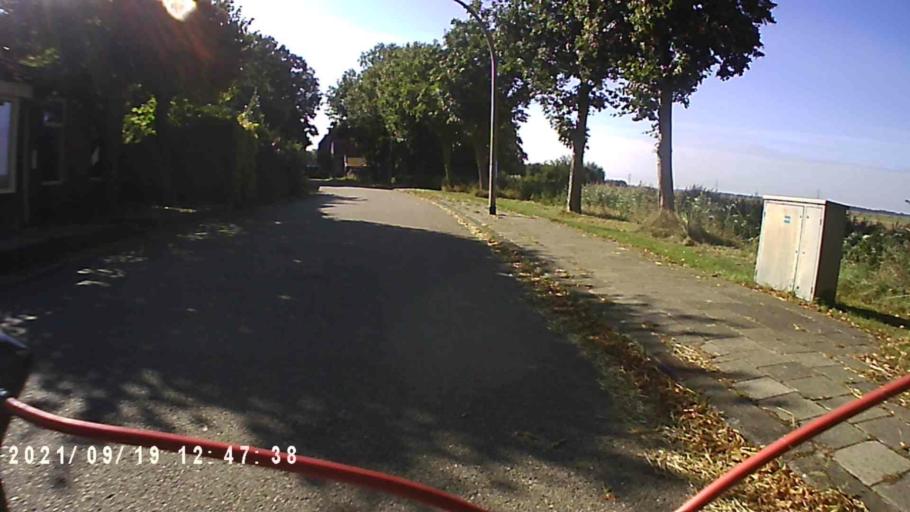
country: NL
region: Groningen
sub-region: Gemeente  Oldambt
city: Winschoten
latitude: 53.2122
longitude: 6.9420
